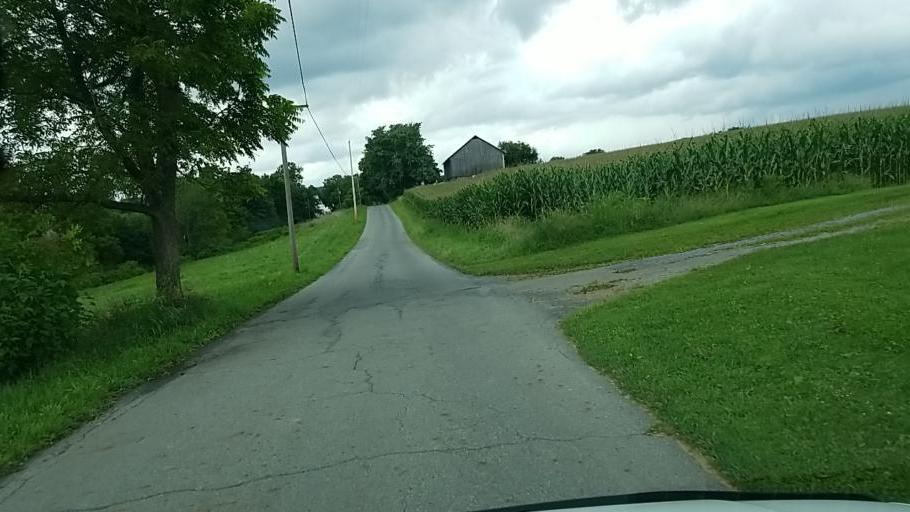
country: US
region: Pennsylvania
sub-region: Dauphin County
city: Elizabethville
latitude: 40.5978
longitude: -76.8031
